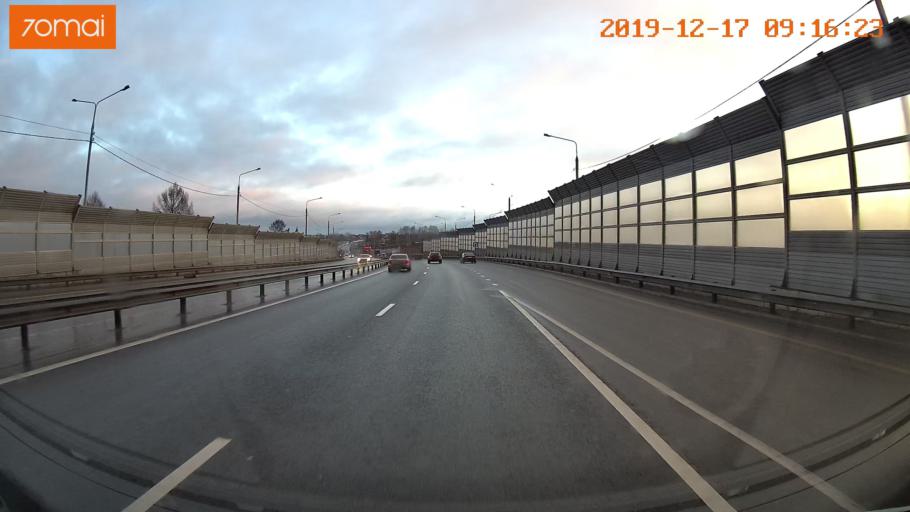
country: RU
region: Vladimir
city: Lakinsk
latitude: 56.0024
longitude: 39.9162
